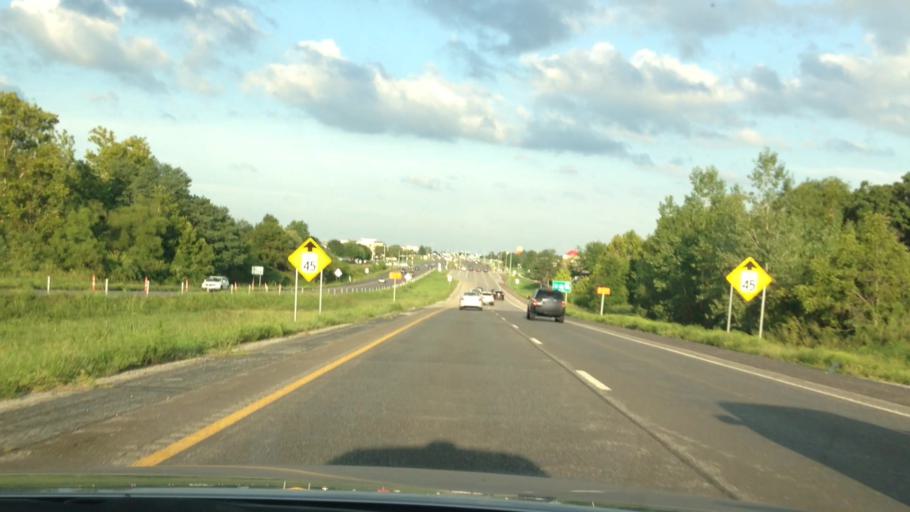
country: US
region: Missouri
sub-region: Clay County
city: Pleasant Valley
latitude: 39.2448
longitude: -94.4714
